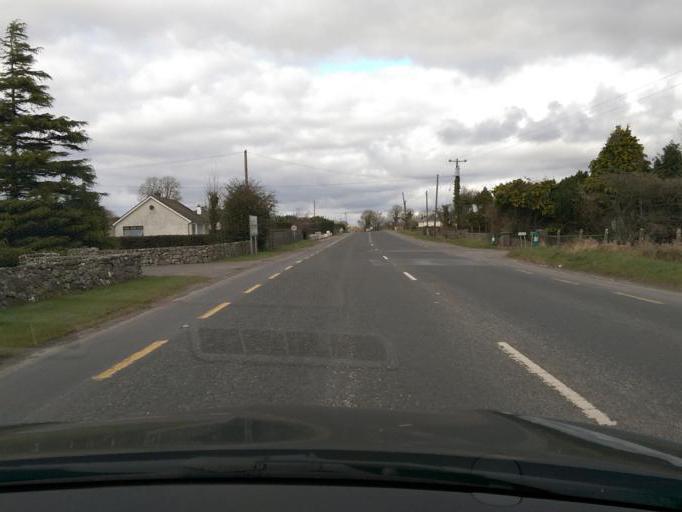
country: IE
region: Leinster
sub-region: An Iarmhi
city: Athlone
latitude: 53.4002
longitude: -7.9884
